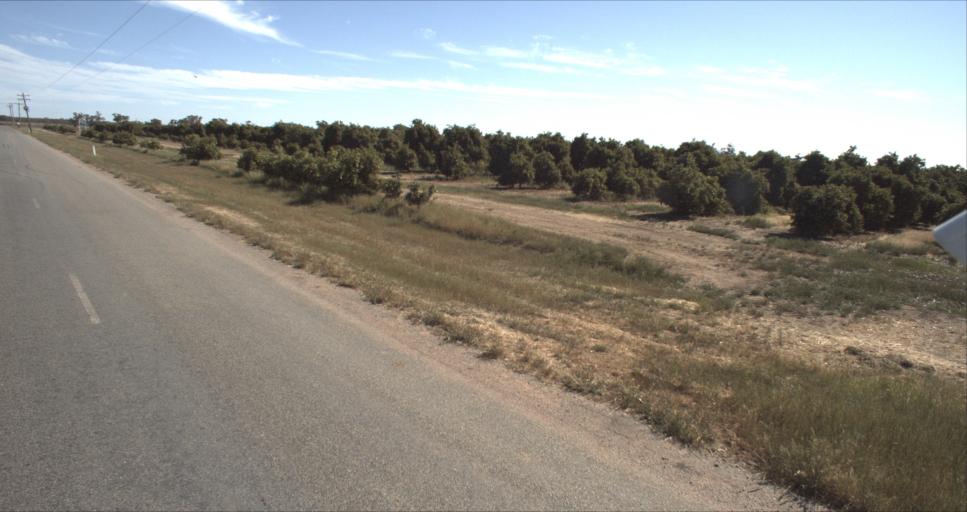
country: AU
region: New South Wales
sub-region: Leeton
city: Leeton
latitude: -34.5847
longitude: 146.3791
